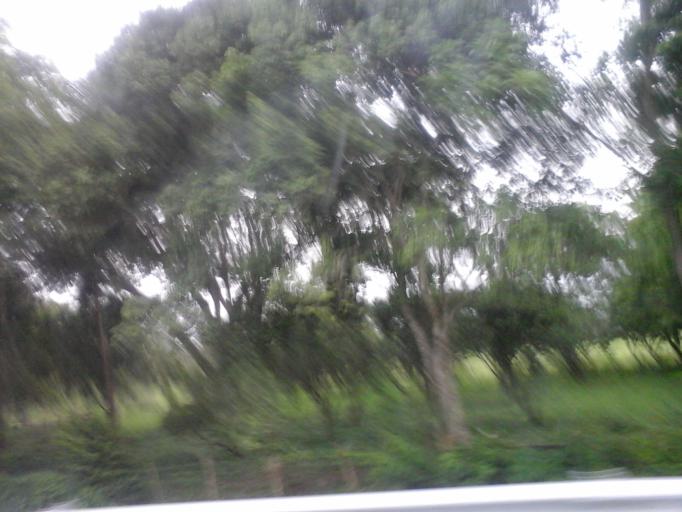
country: CO
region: Bolivar
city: San Pablo
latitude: 10.1366
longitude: -75.2713
